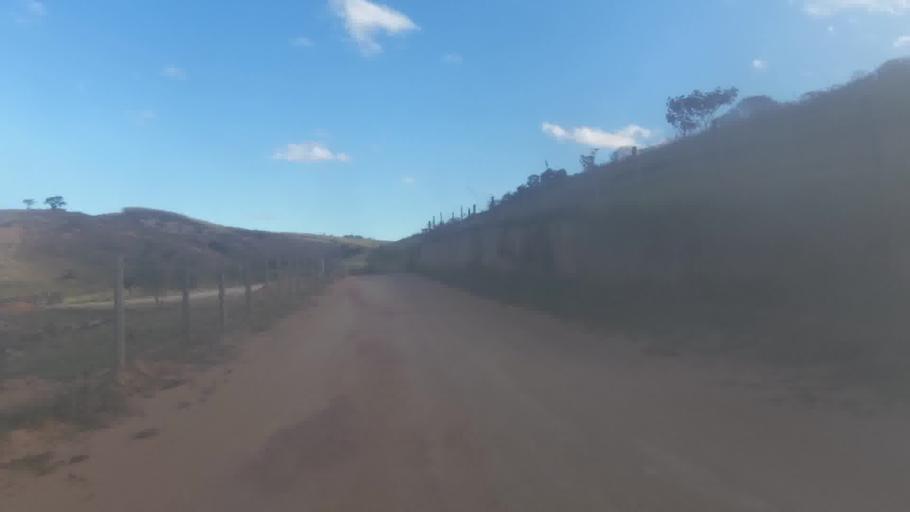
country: BR
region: Espirito Santo
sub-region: Mimoso Do Sul
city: Mimoso do Sul
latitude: -21.0812
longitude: -41.1461
